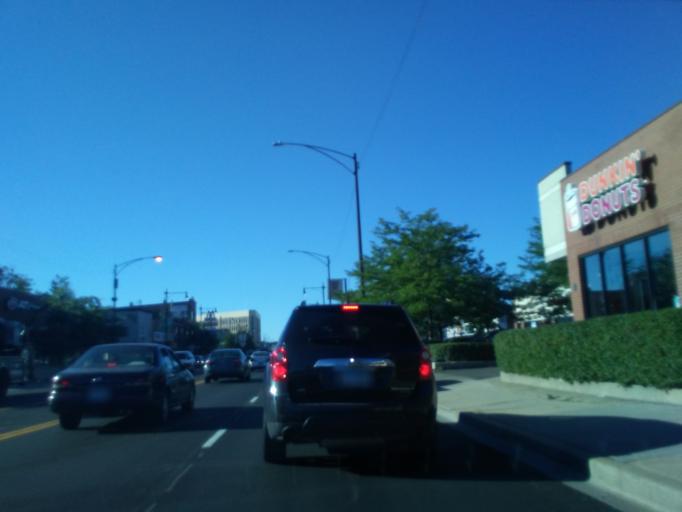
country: US
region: Illinois
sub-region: Cook County
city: Lincolnwood
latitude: 41.9509
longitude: -87.7472
